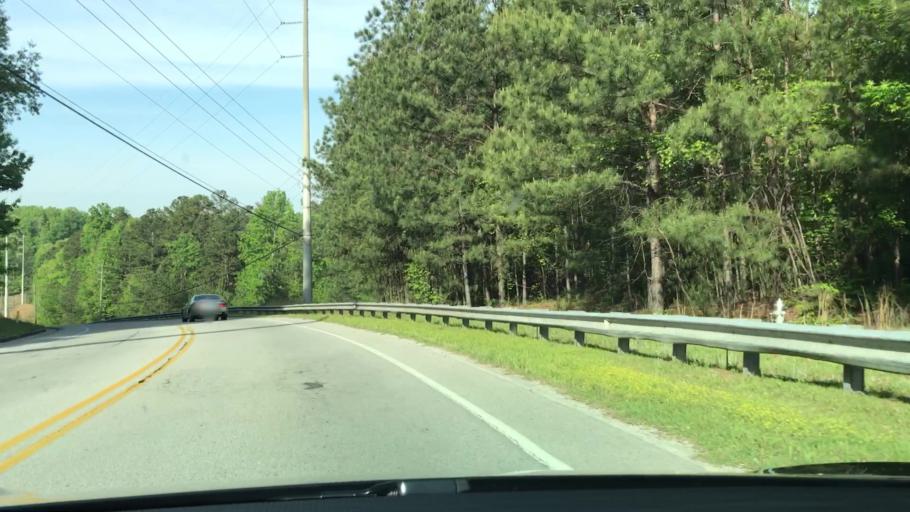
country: US
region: Georgia
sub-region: Gwinnett County
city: Sugar Hill
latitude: 34.1480
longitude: -84.0504
